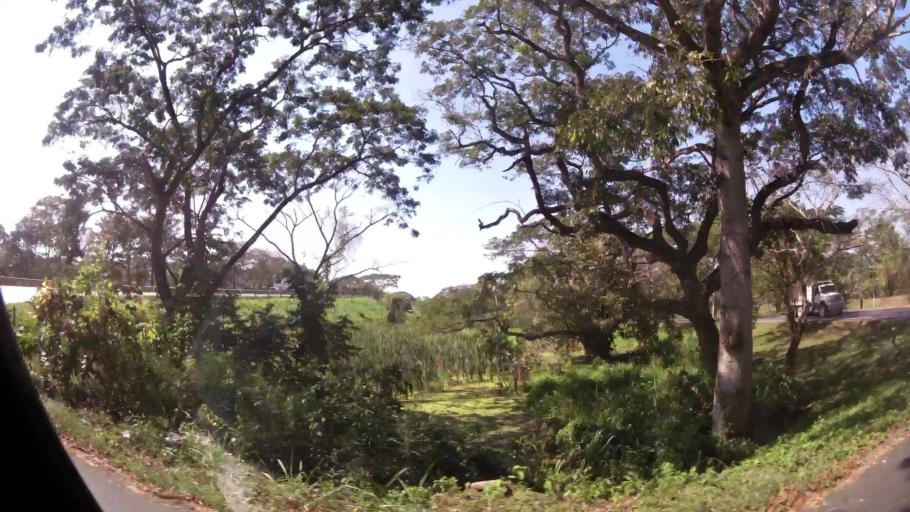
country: CO
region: Bolivar
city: Turbaco
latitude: 10.3718
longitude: -75.4538
